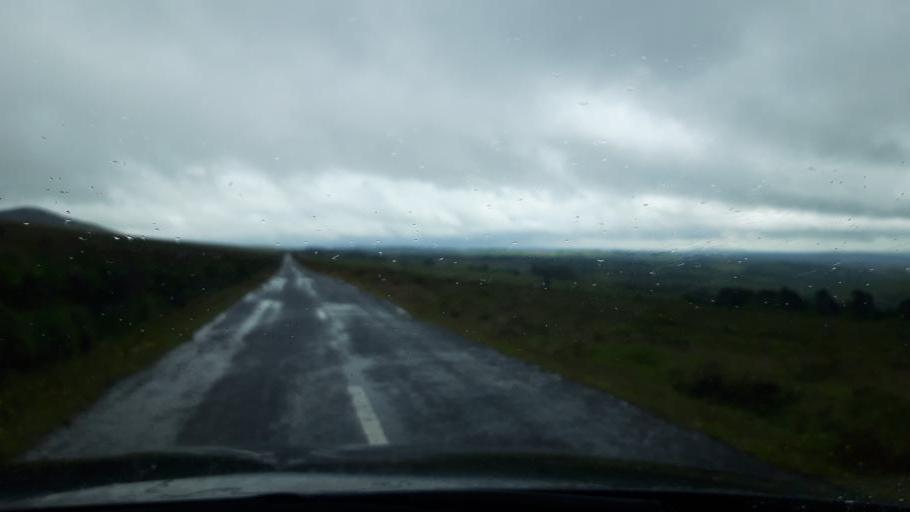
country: IE
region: Munster
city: Cahir
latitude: 52.2175
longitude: -7.9353
